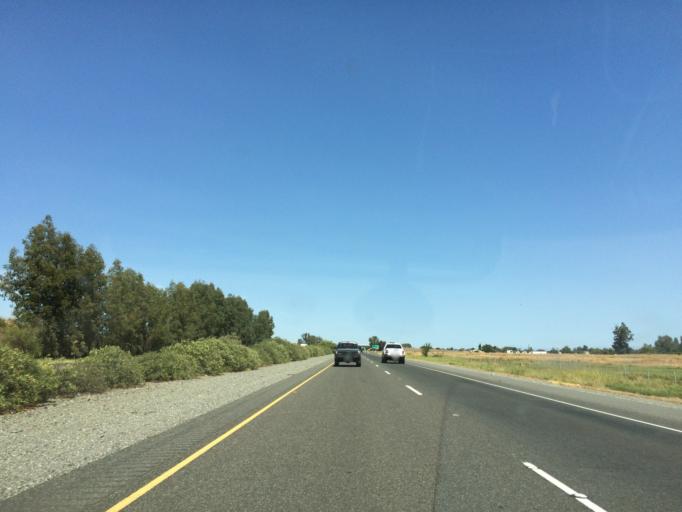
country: US
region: California
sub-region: Glenn County
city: Orland
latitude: 39.7768
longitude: -122.2046
